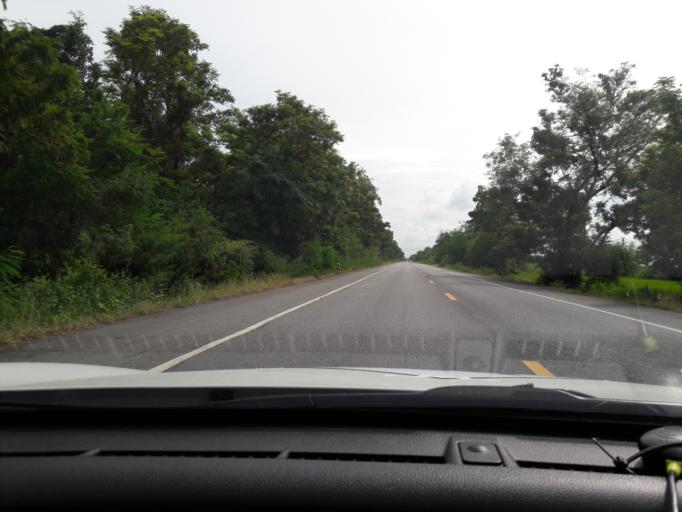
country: TH
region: Nakhon Sawan
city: Phai Sali
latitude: 15.5148
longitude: 100.5450
